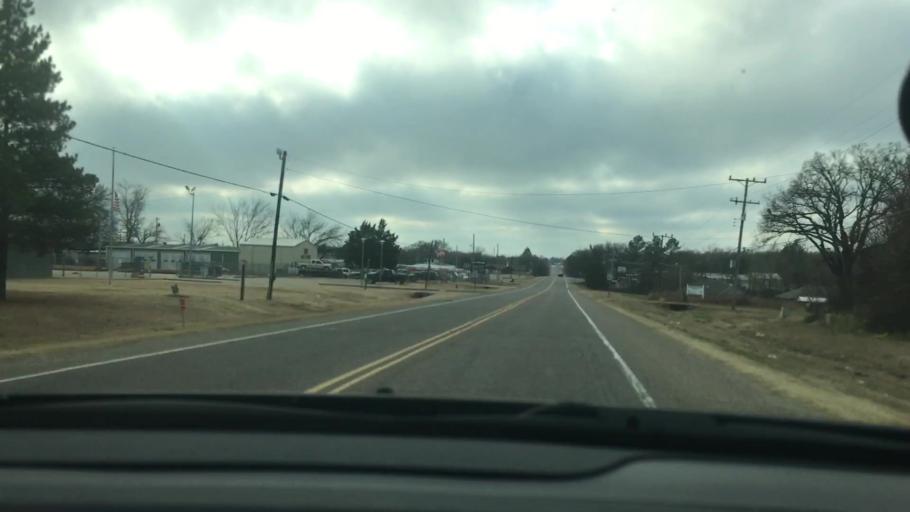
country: US
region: Oklahoma
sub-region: Bryan County
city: Durant
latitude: 34.0162
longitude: -96.3730
